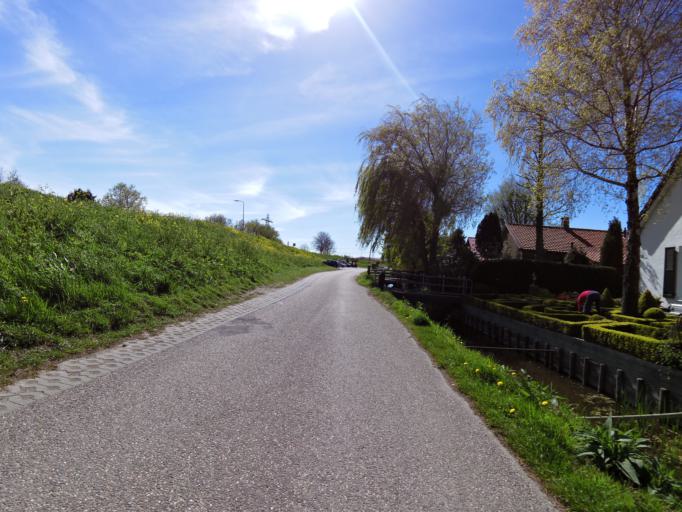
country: NL
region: South Holland
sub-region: Gemeente Brielle
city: Brielle
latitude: 51.9214
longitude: 4.1269
